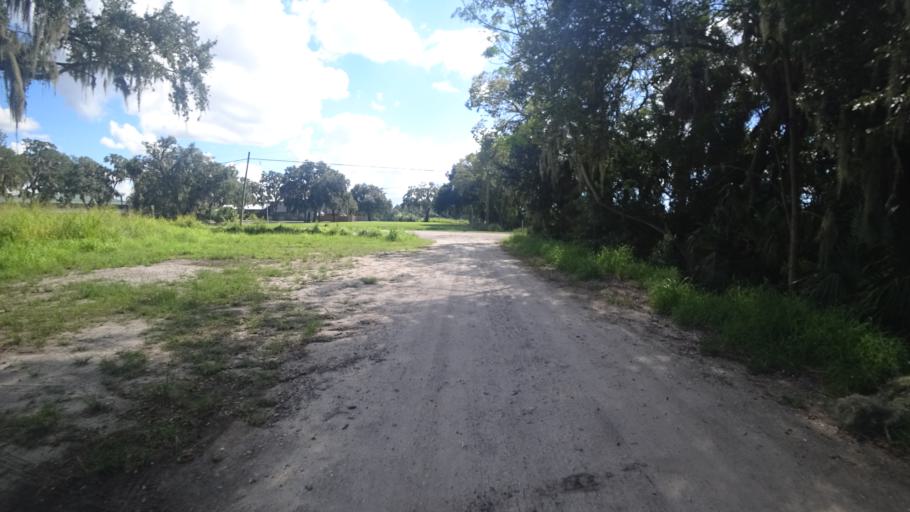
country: US
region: Florida
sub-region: Manatee County
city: Ellenton
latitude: 27.5292
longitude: -82.5156
